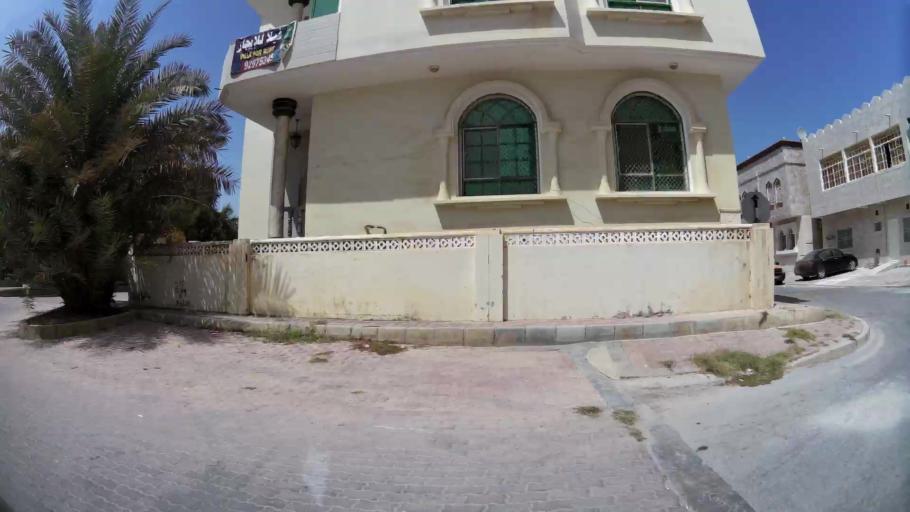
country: OM
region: Zufar
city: Salalah
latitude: 17.0104
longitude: 54.0712
